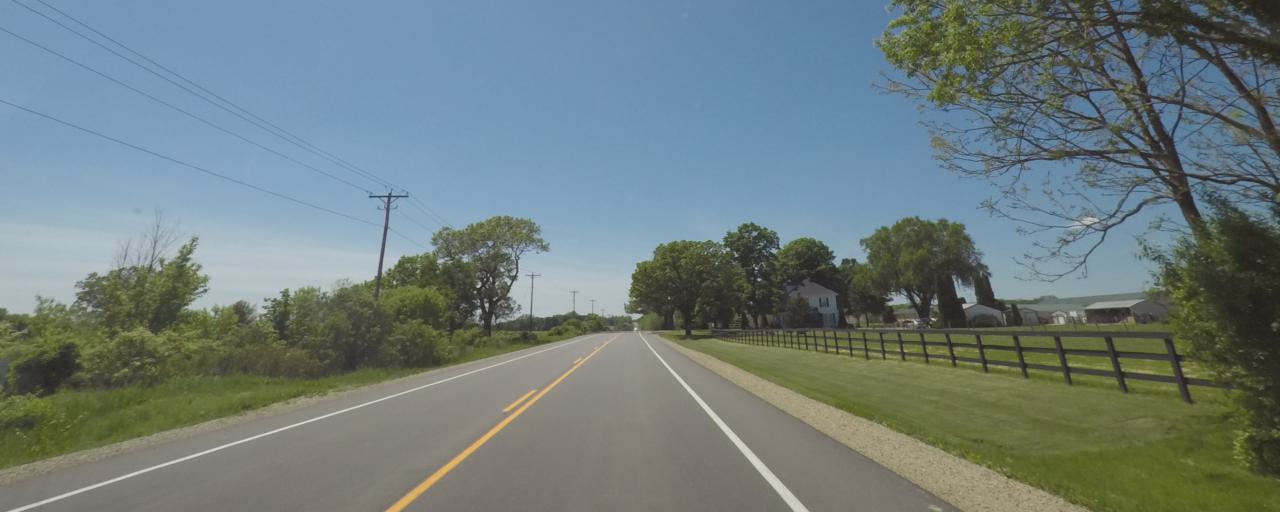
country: US
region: Wisconsin
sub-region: Dane County
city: Fitchburg
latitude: 42.9504
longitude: -89.4260
